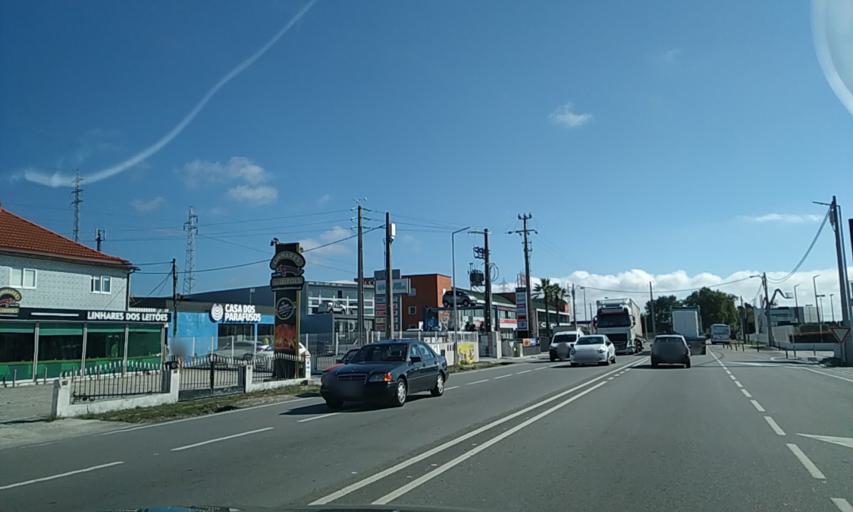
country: PT
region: Aveiro
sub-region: Aveiro
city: Aveiro
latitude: 40.6632
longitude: -8.6119
